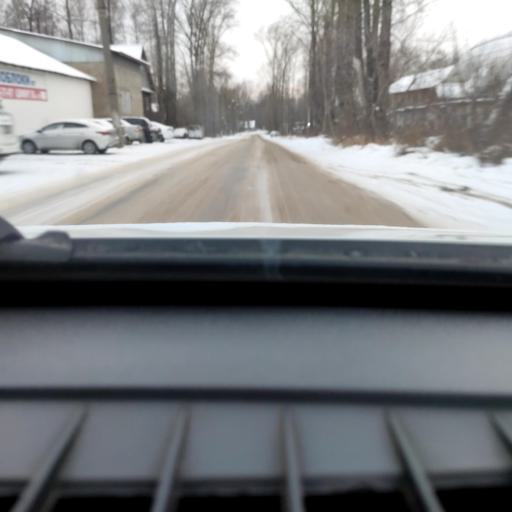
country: RU
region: Perm
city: Perm
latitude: 58.0970
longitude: 56.3699
